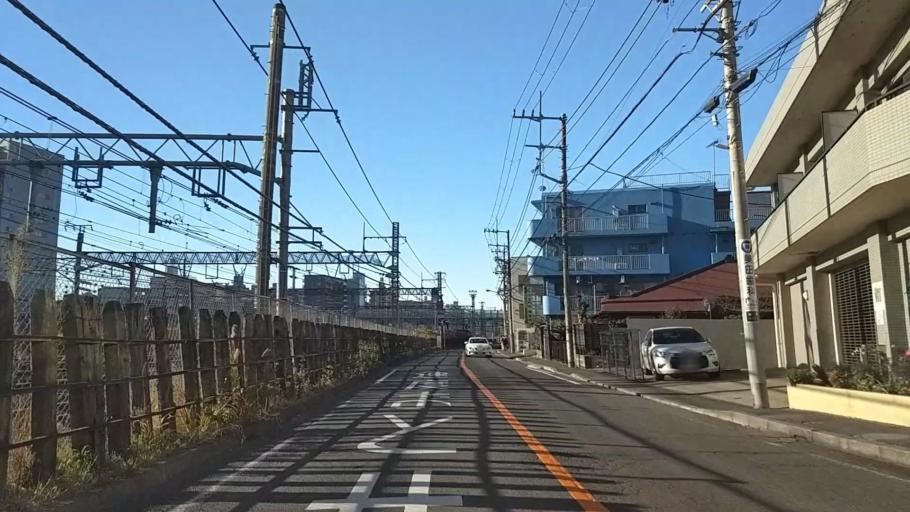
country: JP
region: Kanagawa
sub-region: Kawasaki-shi
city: Kawasaki
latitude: 35.5021
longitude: 139.6738
